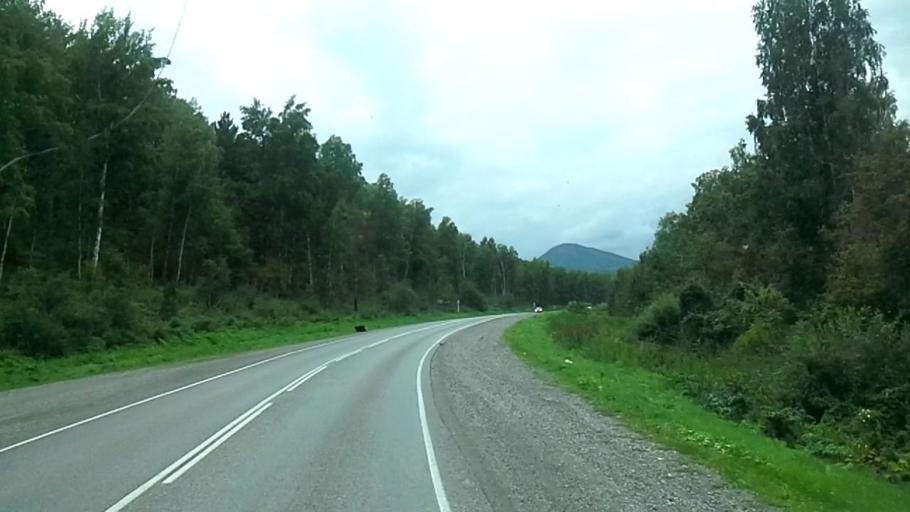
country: RU
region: Altay
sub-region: Mayminskiy Rayon
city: Manzherok
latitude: 51.8593
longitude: 85.7583
